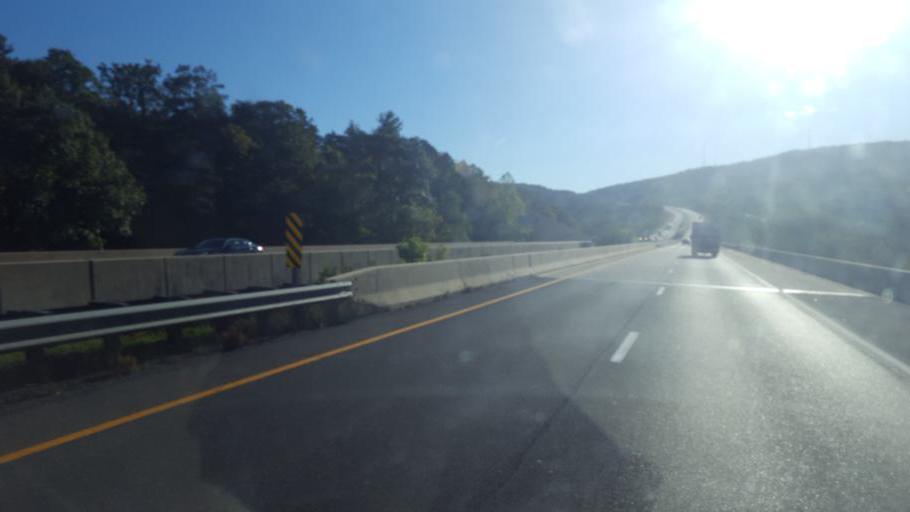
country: US
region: Maryland
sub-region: Allegany County
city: Cumberland
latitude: 39.6971
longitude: -78.5539
